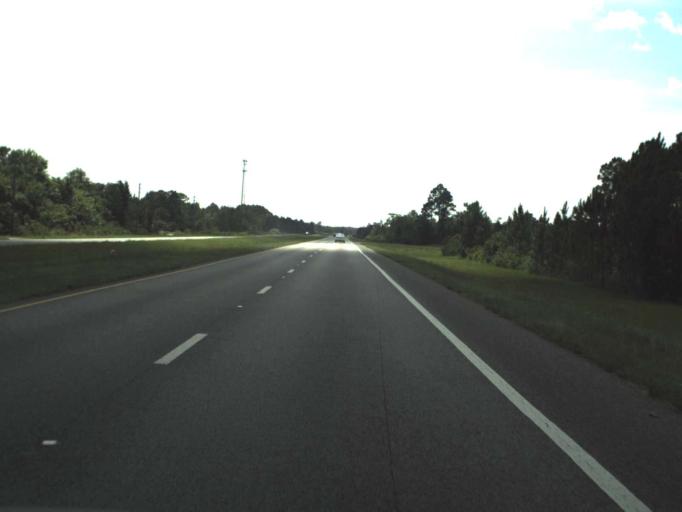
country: US
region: Florida
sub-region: Volusia County
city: Samsula-Spruce Creek
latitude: 29.0255
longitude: -81.1339
